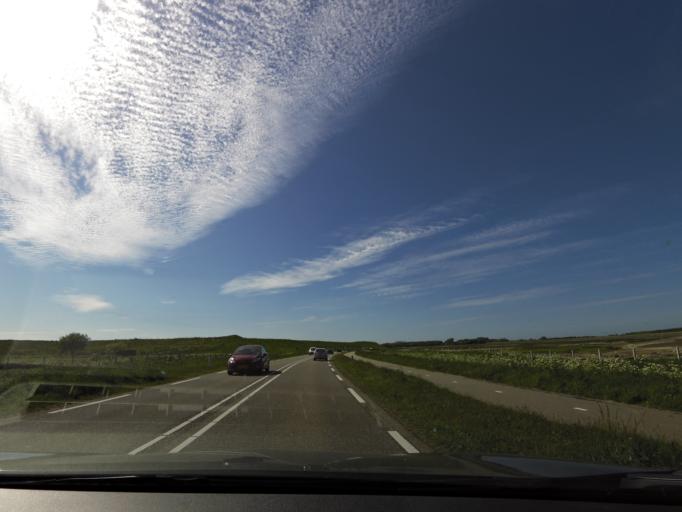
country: NL
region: Zeeland
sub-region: Schouwen-Duiveland
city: Scharendijke
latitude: 51.6925
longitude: 3.8309
